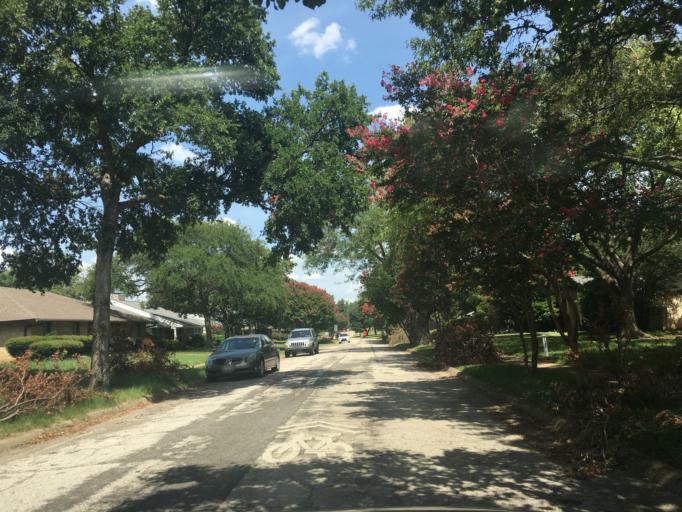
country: US
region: Texas
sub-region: Dallas County
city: Farmers Branch
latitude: 32.9177
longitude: -96.8499
